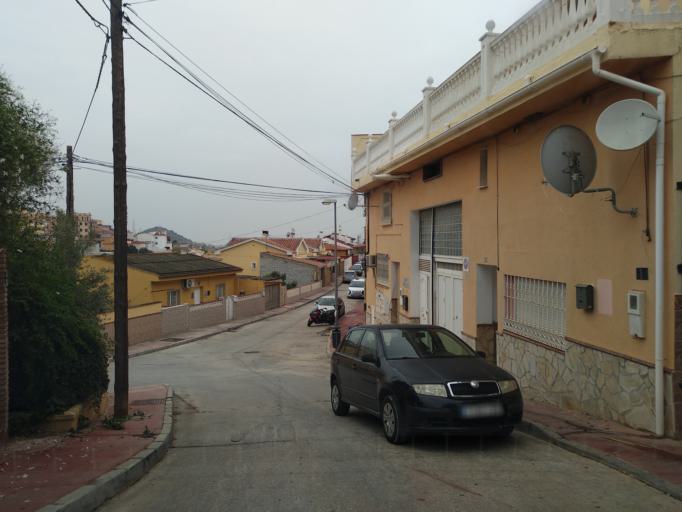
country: ES
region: Andalusia
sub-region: Provincia de Malaga
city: Malaga
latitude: 36.7471
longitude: -4.4779
